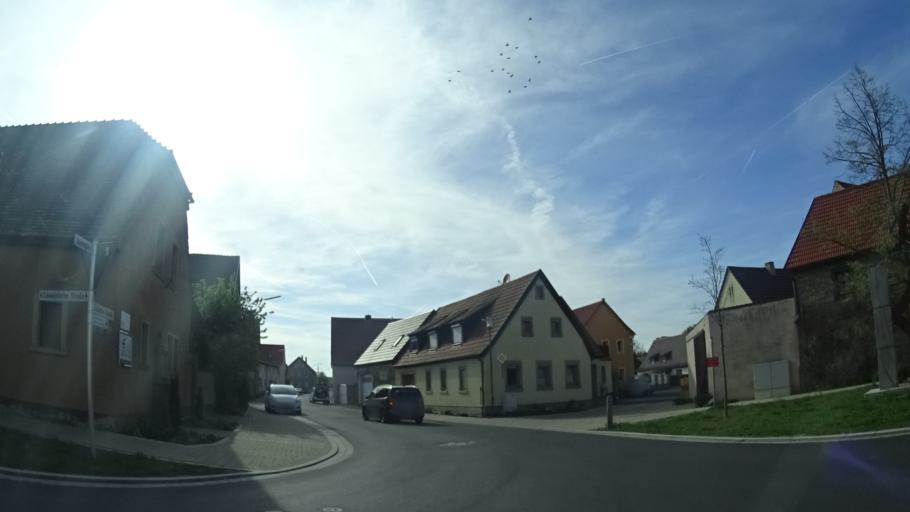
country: DE
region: Bavaria
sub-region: Regierungsbezirk Unterfranken
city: Kolitzheim
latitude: 49.9197
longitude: 10.2364
